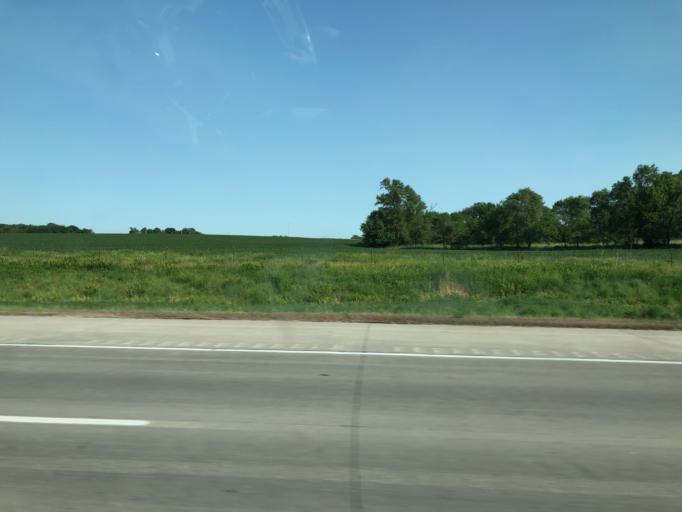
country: US
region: Nebraska
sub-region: Saunders County
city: Ashland
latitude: 40.9593
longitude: -96.4075
